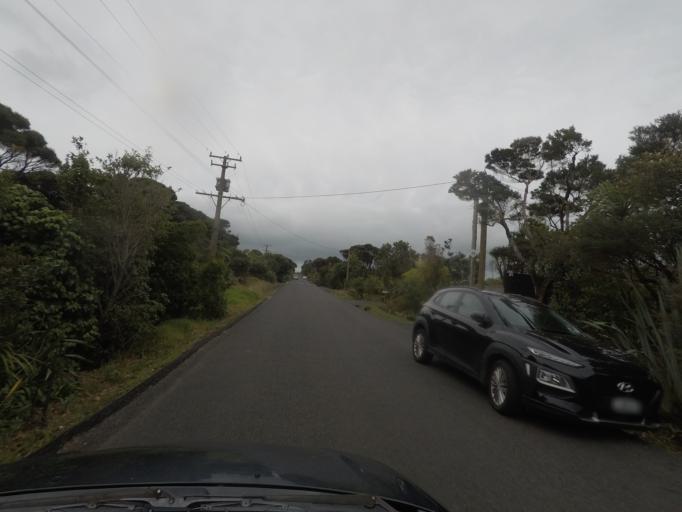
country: NZ
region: Auckland
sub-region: Auckland
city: Muriwai Beach
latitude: -36.9678
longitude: 174.4773
